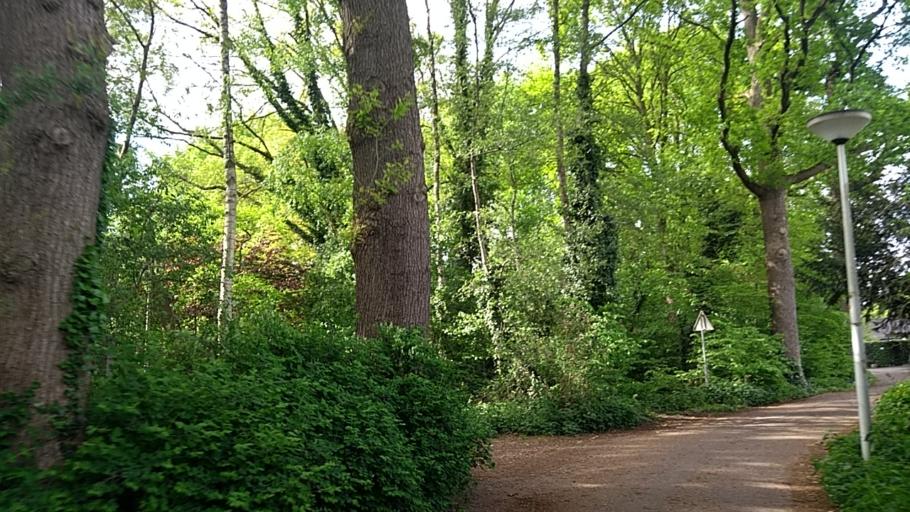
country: NL
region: Overijssel
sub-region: Gemeente Almelo
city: Almelo
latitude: 52.3653
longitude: 6.6601
